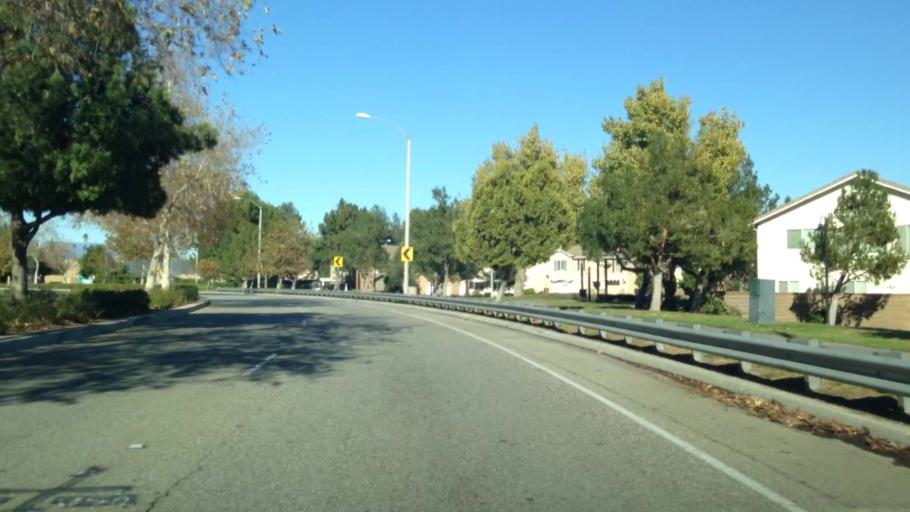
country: US
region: California
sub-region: Riverside County
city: Home Gardens
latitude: 33.9132
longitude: -117.4922
